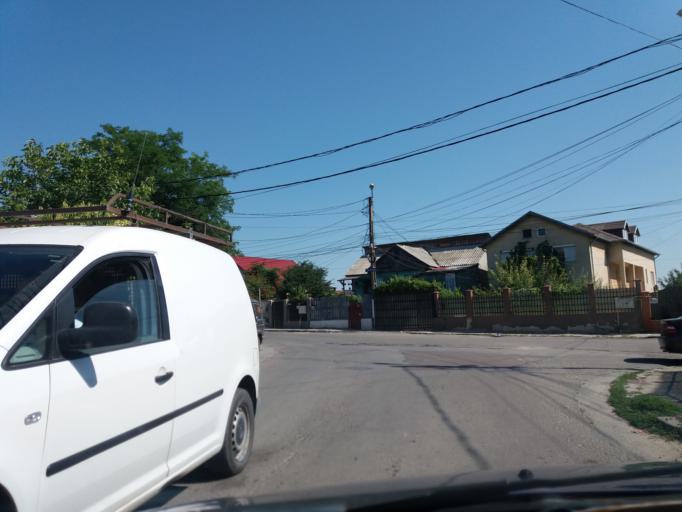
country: RO
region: Constanta
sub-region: Comuna Navodari
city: Navodari
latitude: 44.3299
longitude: 28.6110
